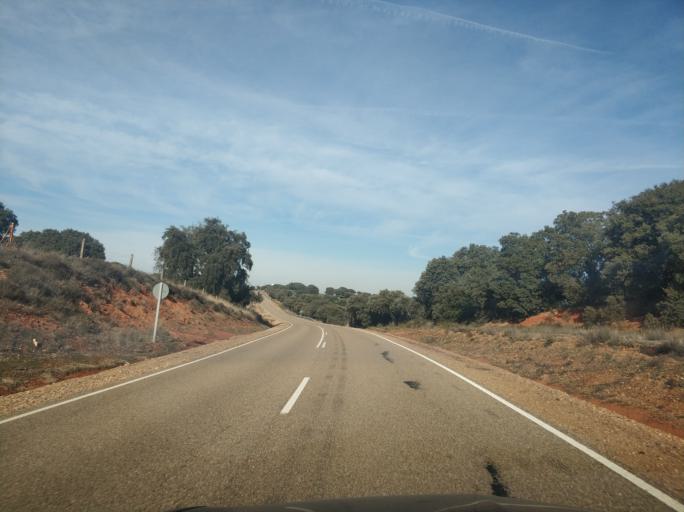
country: ES
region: Castille and Leon
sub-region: Provincia de Salamanca
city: Zarapicos
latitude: 41.0046
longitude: -5.8324
